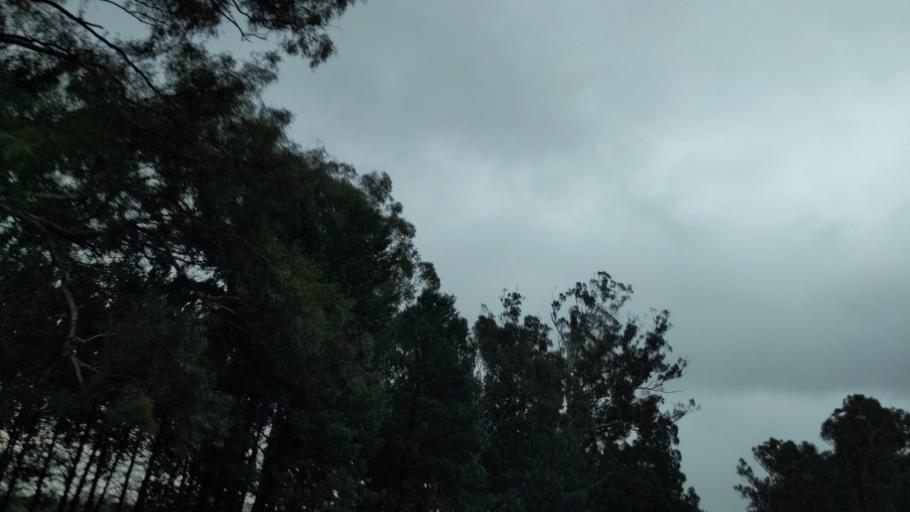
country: AU
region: New South Wales
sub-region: Coolamon
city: Coolamon
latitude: -34.9095
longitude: 147.2778
